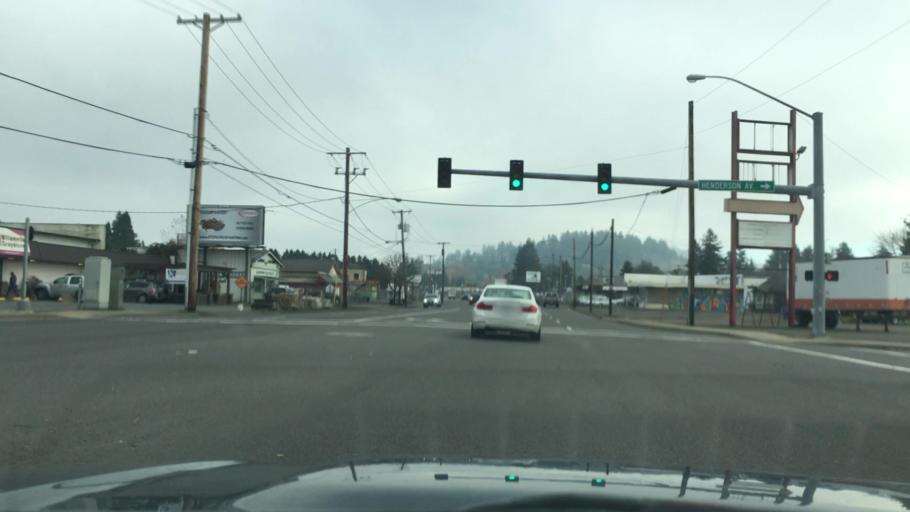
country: US
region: Oregon
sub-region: Lane County
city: Springfield
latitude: 44.0454
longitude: -123.0387
